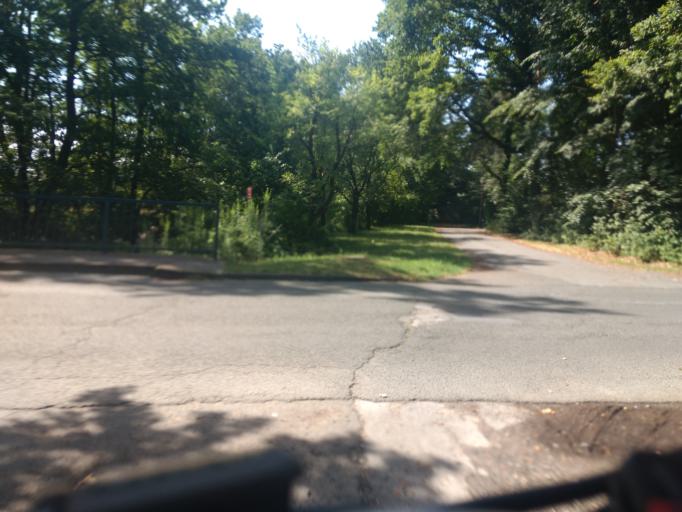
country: DE
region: North Rhine-Westphalia
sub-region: Regierungsbezirk Detmold
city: Hovelhof
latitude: 51.7654
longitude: 8.6636
